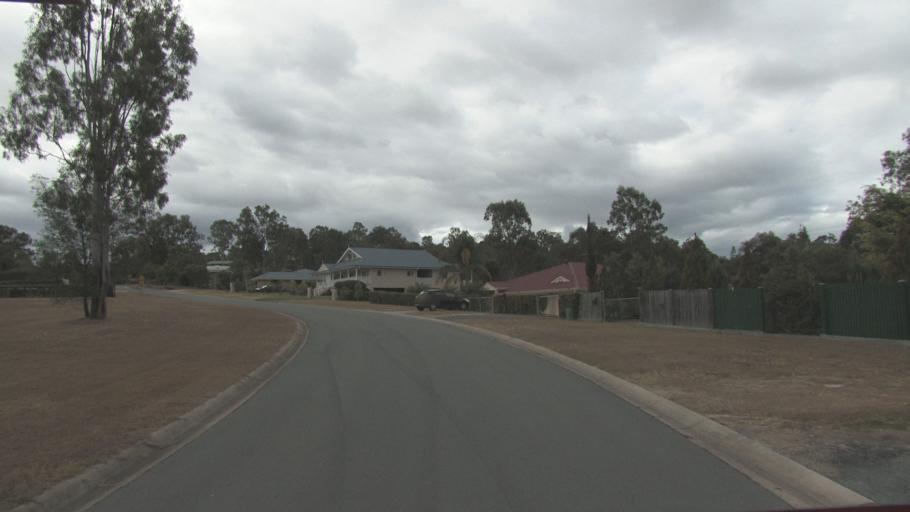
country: AU
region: Queensland
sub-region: Logan
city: Cedar Vale
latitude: -27.8743
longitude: 153.0689
